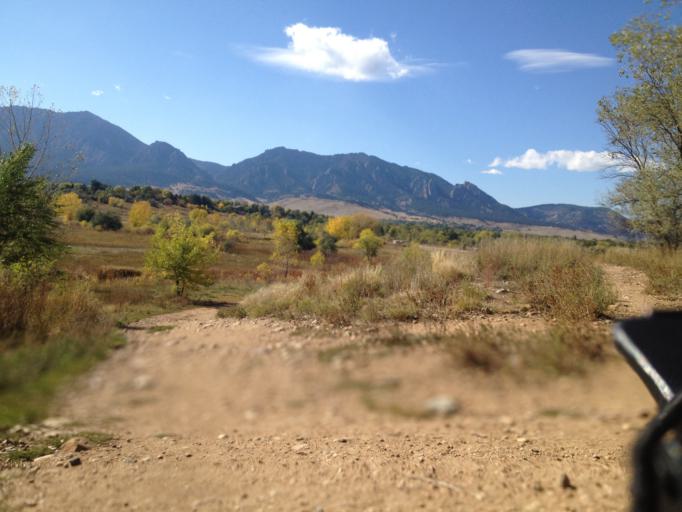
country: US
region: Colorado
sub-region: Boulder County
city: Boulder
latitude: 39.9786
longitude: -105.2282
